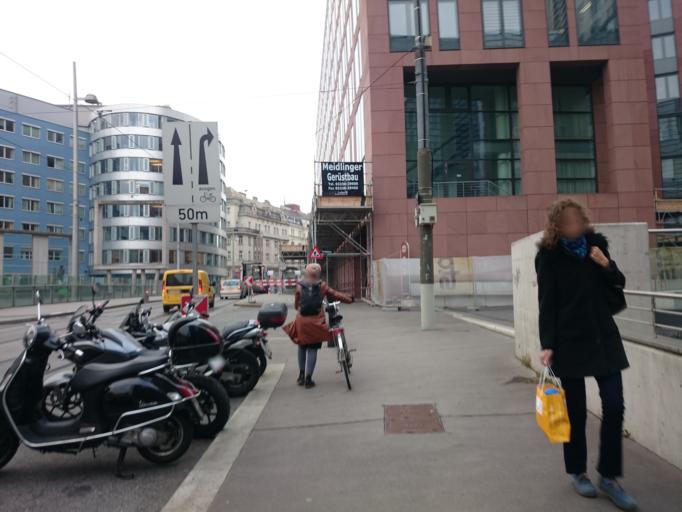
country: AT
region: Vienna
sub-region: Wien Stadt
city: Vienna
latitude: 48.2087
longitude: 16.3866
